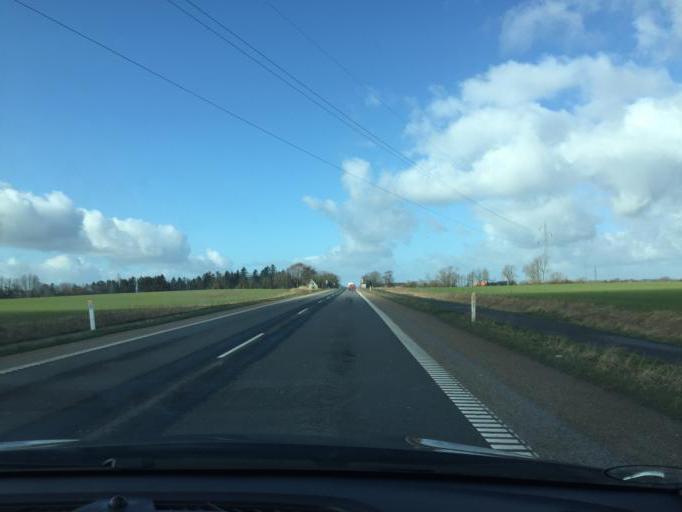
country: DK
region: South Denmark
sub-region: Middelfart Kommune
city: Norre Aby
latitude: 55.4859
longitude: 9.8190
